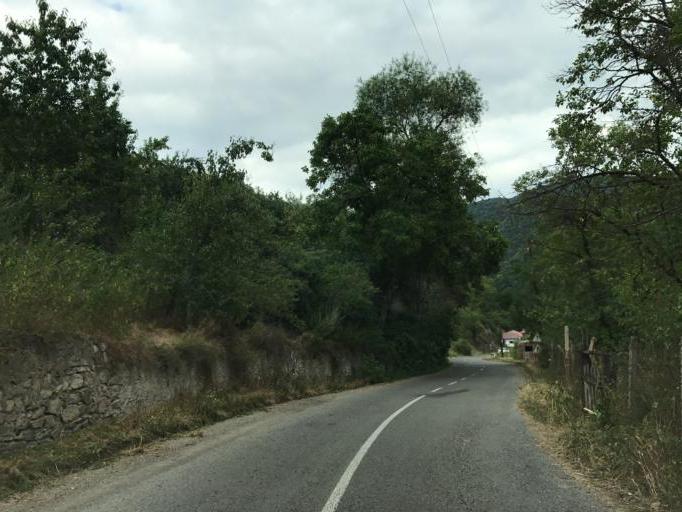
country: AM
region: Tavush
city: Haghartsin
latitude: 40.7313
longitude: 45.0051
